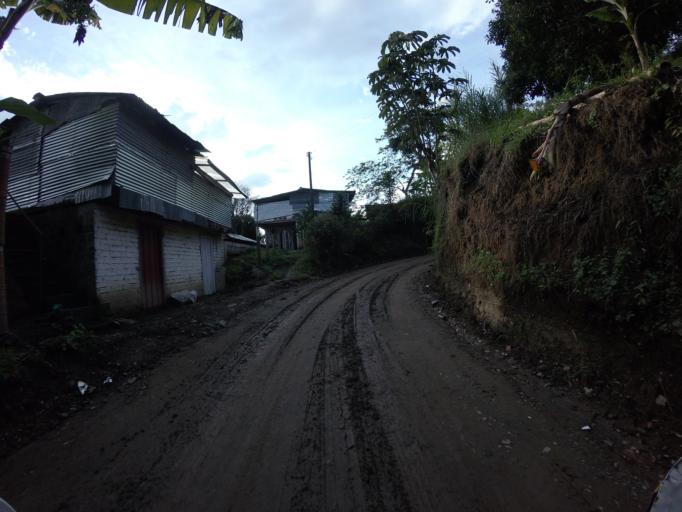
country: CO
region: Valle del Cauca
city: Ulloa
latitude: 4.7064
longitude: -75.7094
